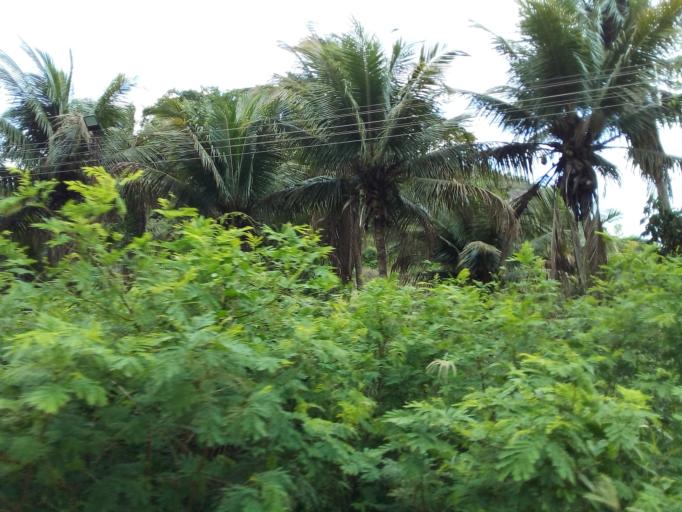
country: BR
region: Espirito Santo
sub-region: Joao Neiva
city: Joao Neiva
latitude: -19.7492
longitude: -40.3663
